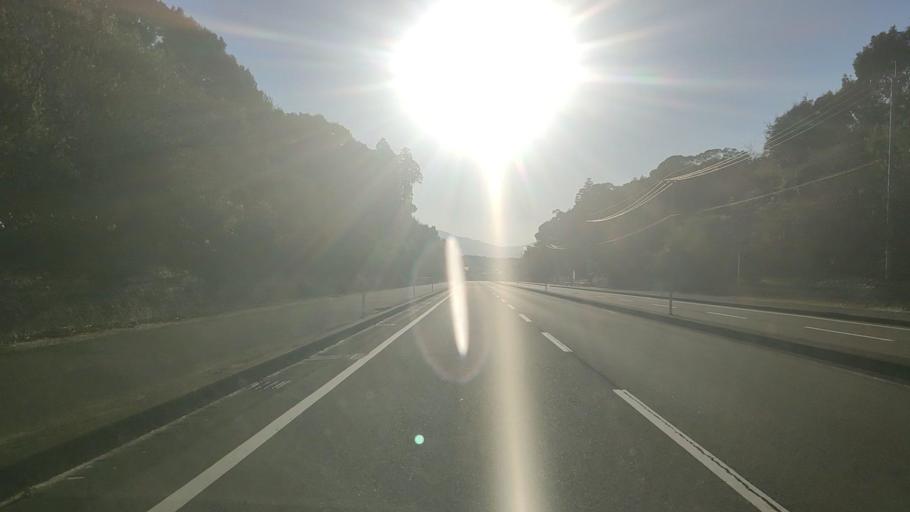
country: JP
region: Miyazaki
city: Miyazaki-shi
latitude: 31.8847
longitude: 131.3993
